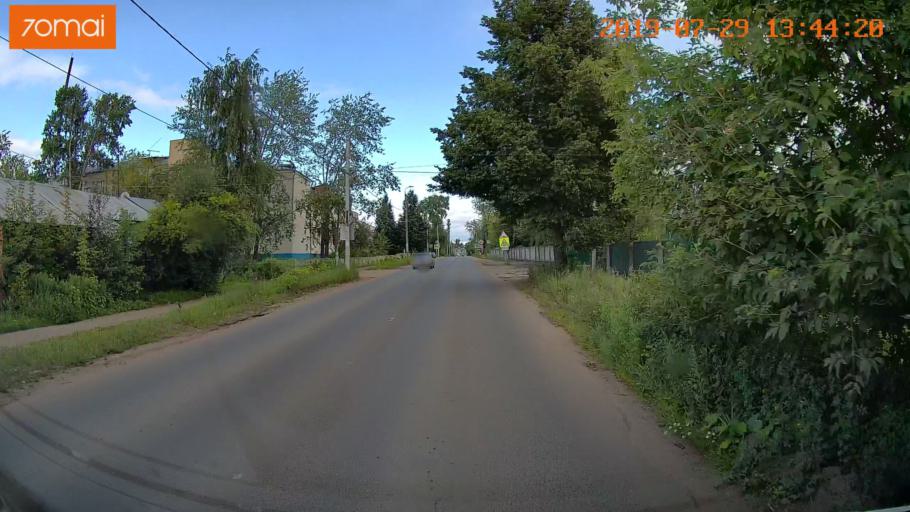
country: RU
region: Ivanovo
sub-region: Gorod Ivanovo
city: Ivanovo
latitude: 57.0094
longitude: 40.9329
